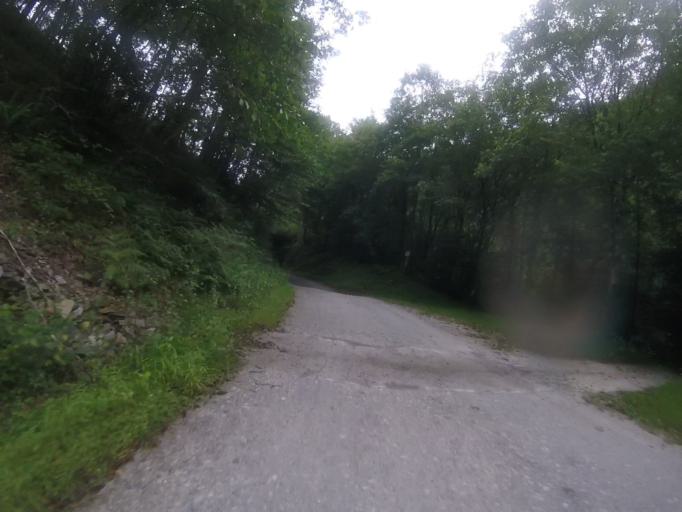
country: ES
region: Navarre
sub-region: Provincia de Navarra
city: Areso
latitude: 43.1181
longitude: -1.9378
